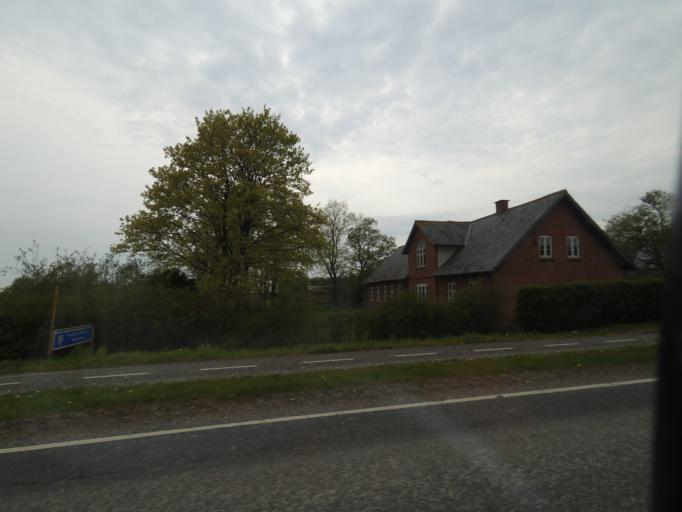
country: DK
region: South Denmark
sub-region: Faaborg-Midtfyn Kommune
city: Arslev
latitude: 55.3096
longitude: 10.4510
